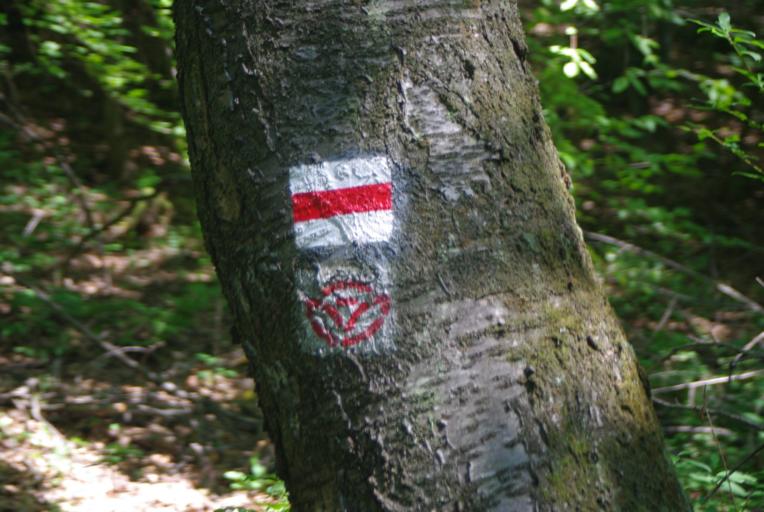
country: HU
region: Borsod-Abauj-Zemplen
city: Gonc
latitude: 48.4094
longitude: 21.3393
